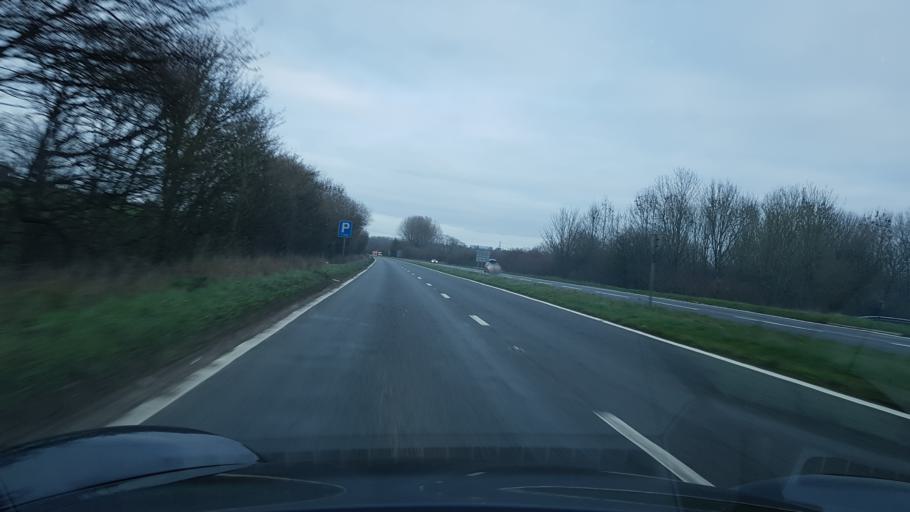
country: GB
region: England
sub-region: Hampshire
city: Alton
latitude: 51.1371
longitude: -0.9772
